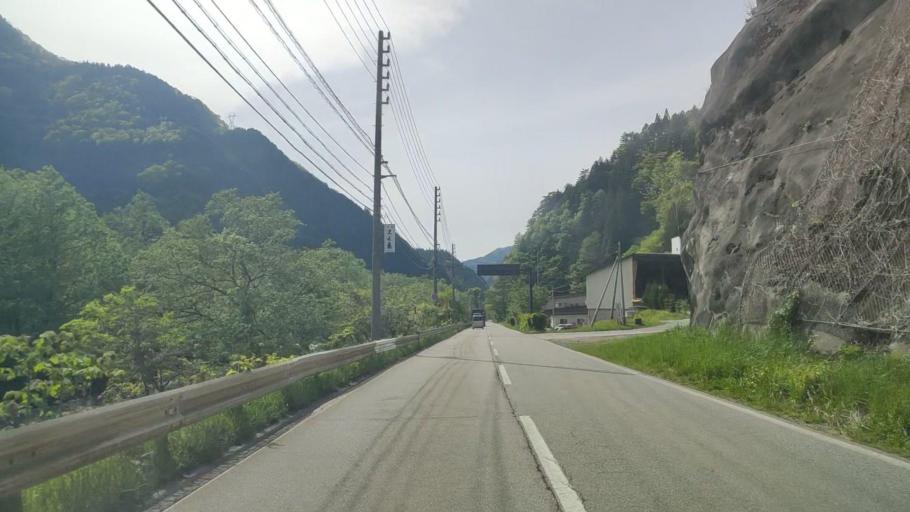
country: JP
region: Gifu
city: Takayama
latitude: 36.2502
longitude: 137.4836
